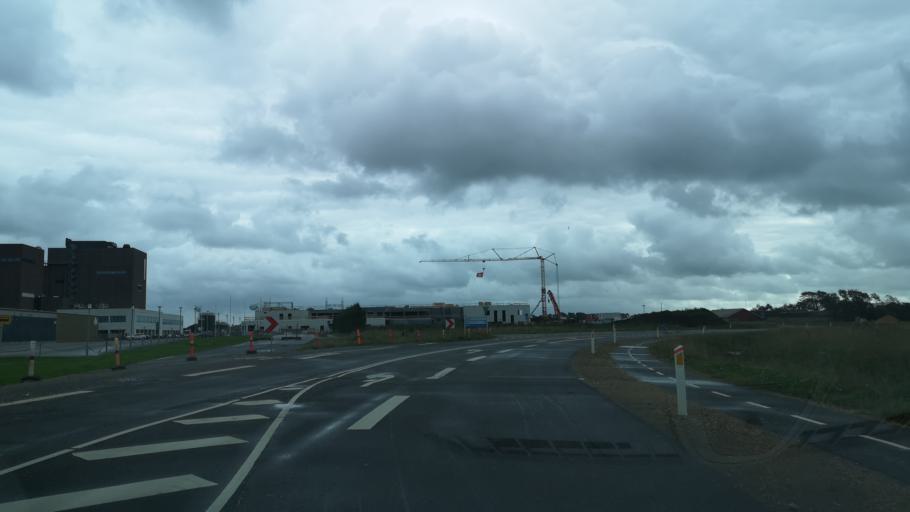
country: DK
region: Central Jutland
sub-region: Ringkobing-Skjern Kommune
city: Videbaek
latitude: 56.0481
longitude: 8.6634
